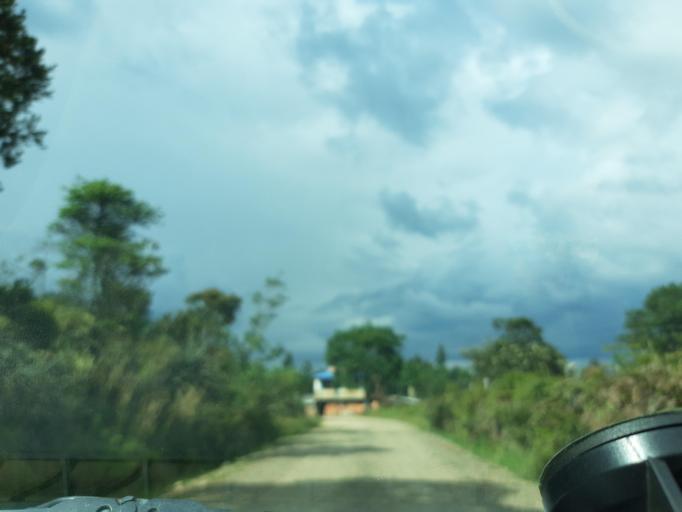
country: CO
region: Boyaca
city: Raquira
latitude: 5.5154
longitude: -73.6664
